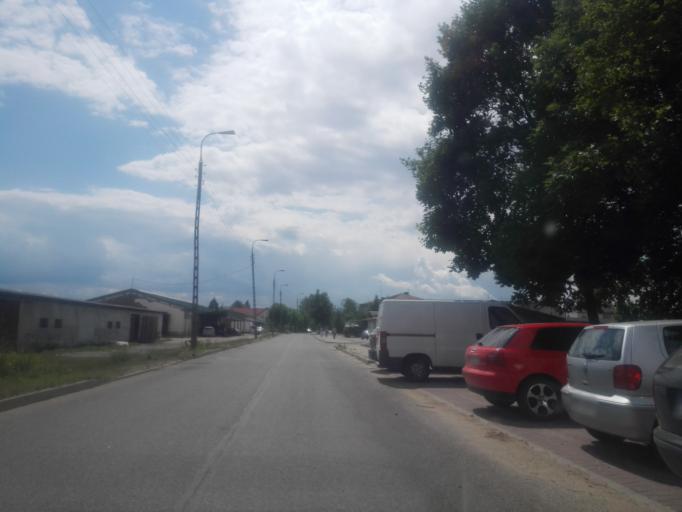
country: PL
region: Podlasie
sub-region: Powiat sejnenski
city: Sejny
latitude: 54.1144
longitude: 23.3530
